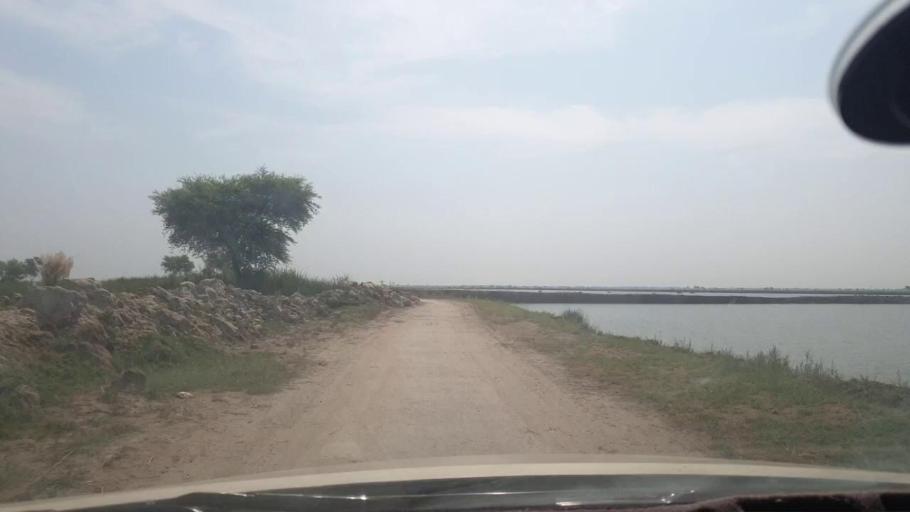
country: PK
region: Sindh
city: Jacobabad
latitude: 28.3106
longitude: 68.4786
